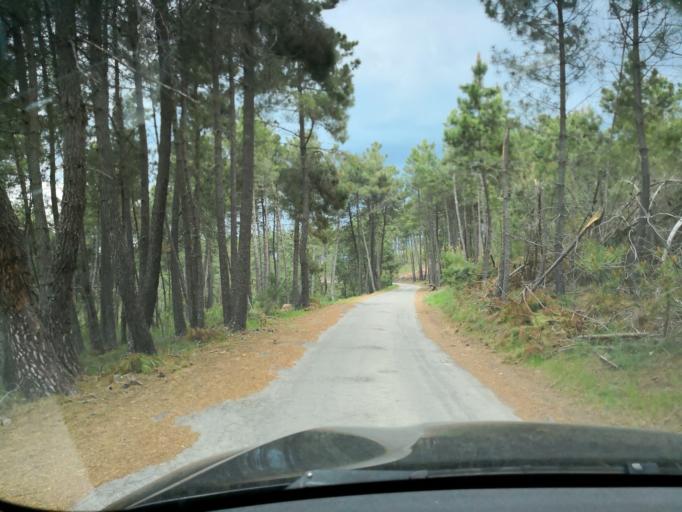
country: PT
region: Vila Real
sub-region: Sabrosa
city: Vilela
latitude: 41.2486
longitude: -7.6578
